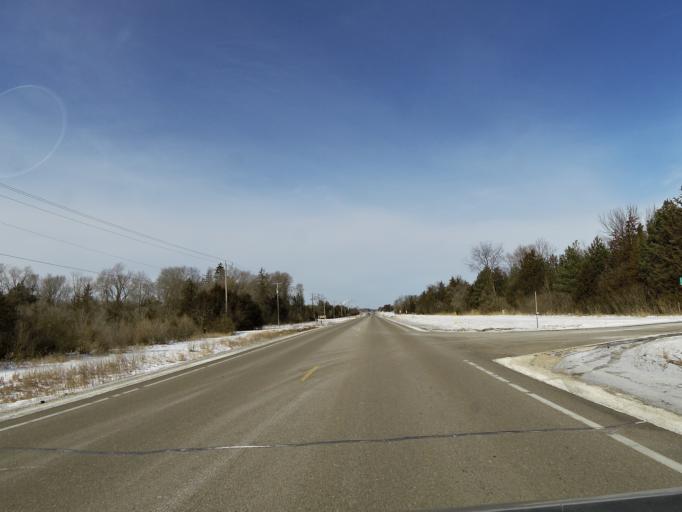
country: US
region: Minnesota
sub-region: Washington County
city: Lake Saint Croix Beach
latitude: 44.9338
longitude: -92.7711
